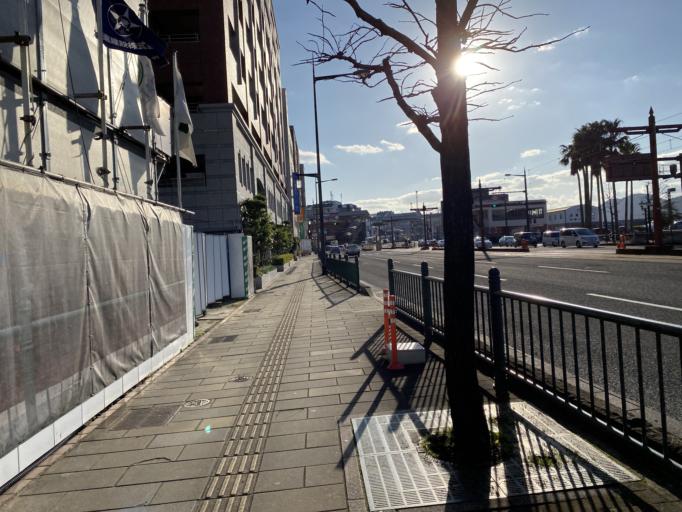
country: JP
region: Nagasaki
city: Nagasaki-shi
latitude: 32.7387
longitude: 129.8713
